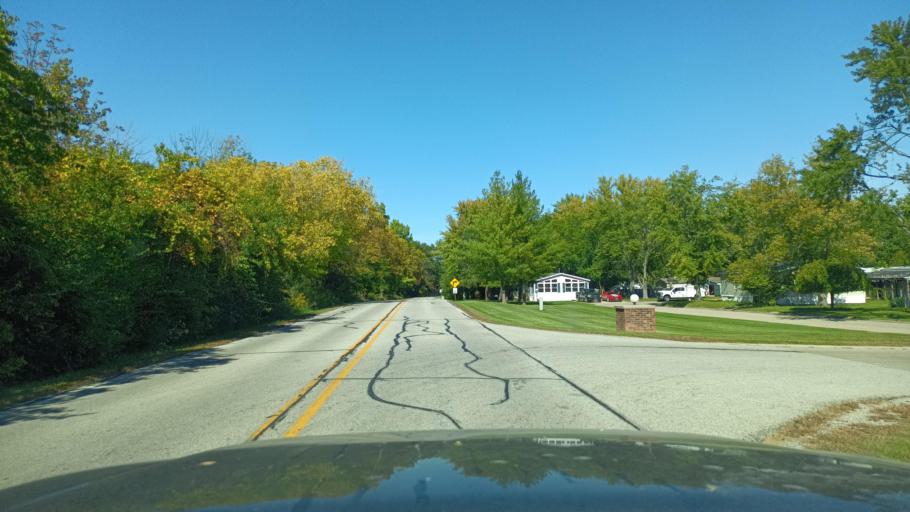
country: US
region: Illinois
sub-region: Champaign County
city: Lake of the Woods
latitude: 40.2093
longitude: -88.3653
